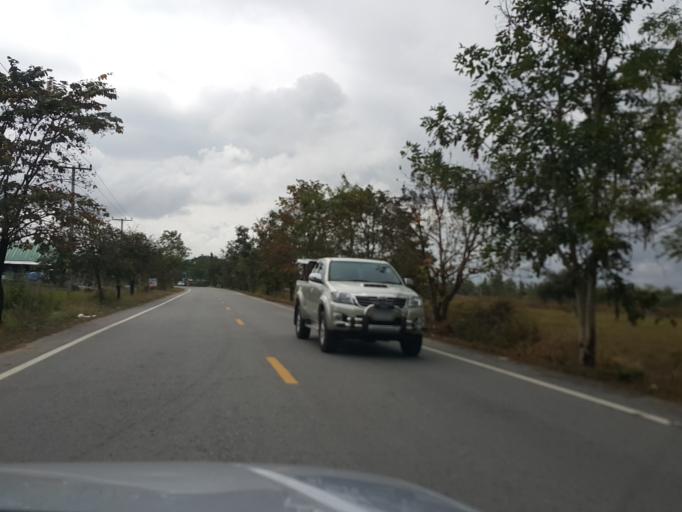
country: TH
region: Lamphun
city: Ban Thi
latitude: 18.6404
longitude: 99.1064
